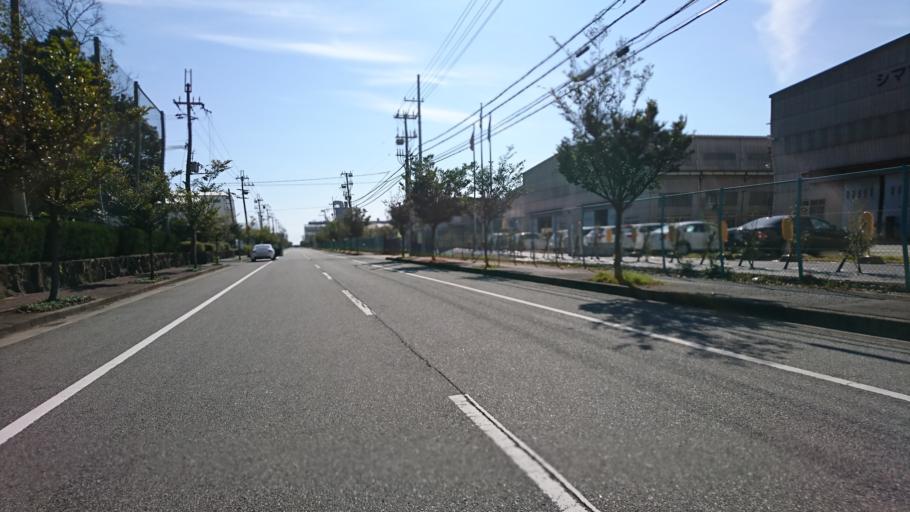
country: JP
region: Hyogo
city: Kakogawacho-honmachi
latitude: 34.7020
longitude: 134.8500
